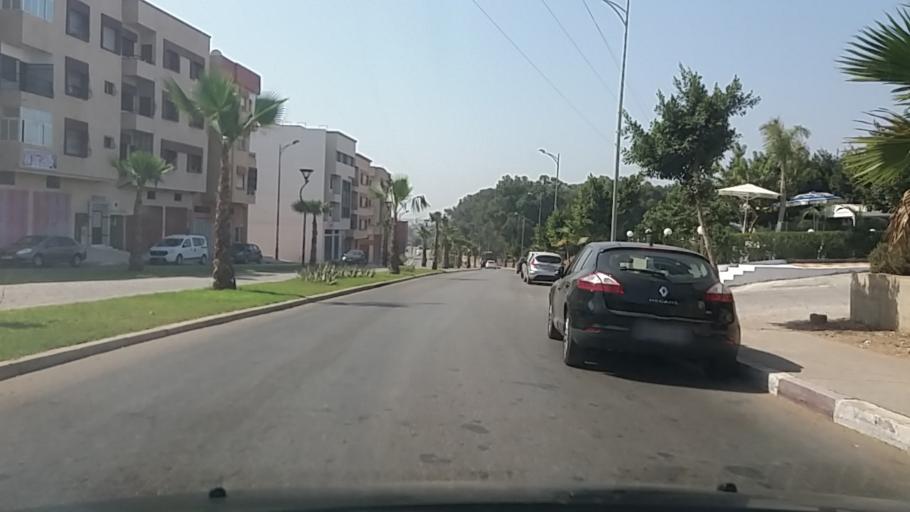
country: MA
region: Gharb-Chrarda-Beni Hssen
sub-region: Kenitra Province
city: Kenitra
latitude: 34.2523
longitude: -6.6149
